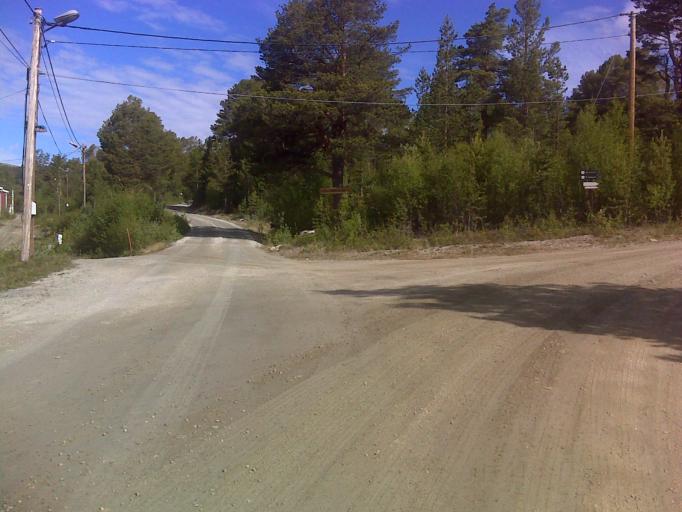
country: NO
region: Hedmark
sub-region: Folldal
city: Folldal
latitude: 62.1416
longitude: 9.9925
